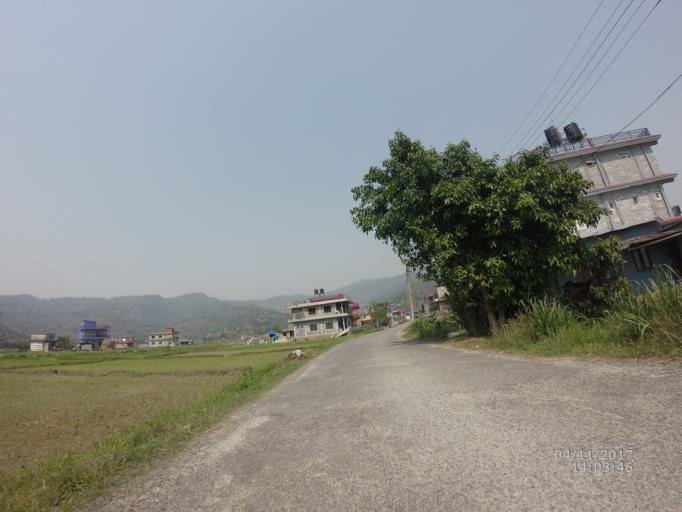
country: NP
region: Western Region
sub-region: Gandaki Zone
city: Pokhara
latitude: 28.1861
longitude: 84.0504
